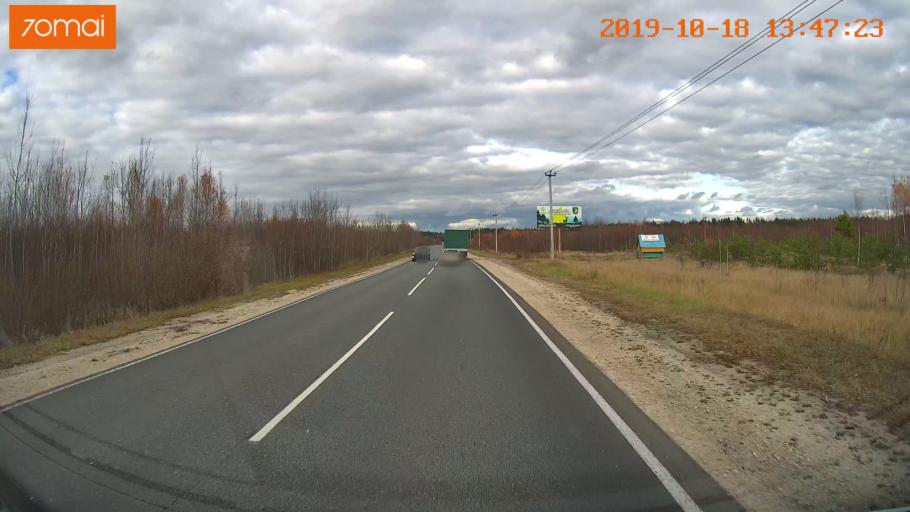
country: RU
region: Rjazan
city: Solotcha
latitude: 54.9739
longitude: 39.9511
